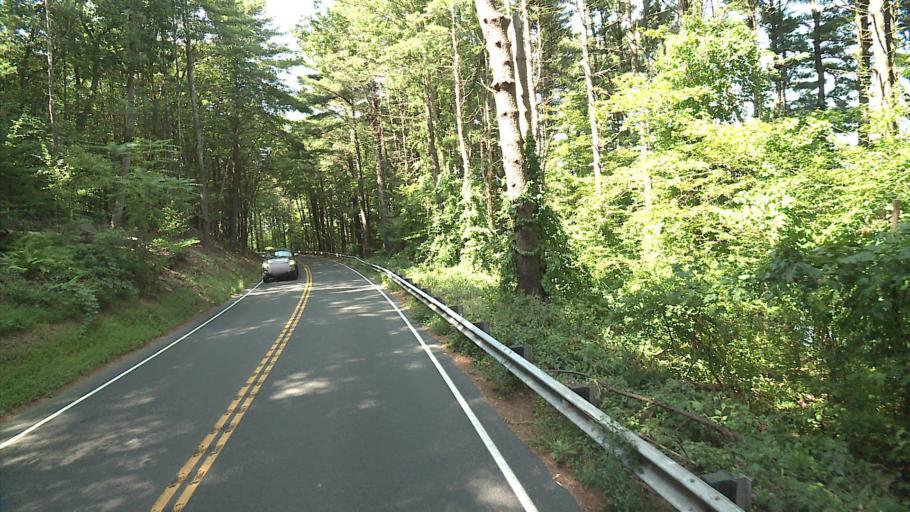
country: US
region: Connecticut
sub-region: Fairfield County
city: Southport
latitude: 41.2210
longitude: -73.3002
